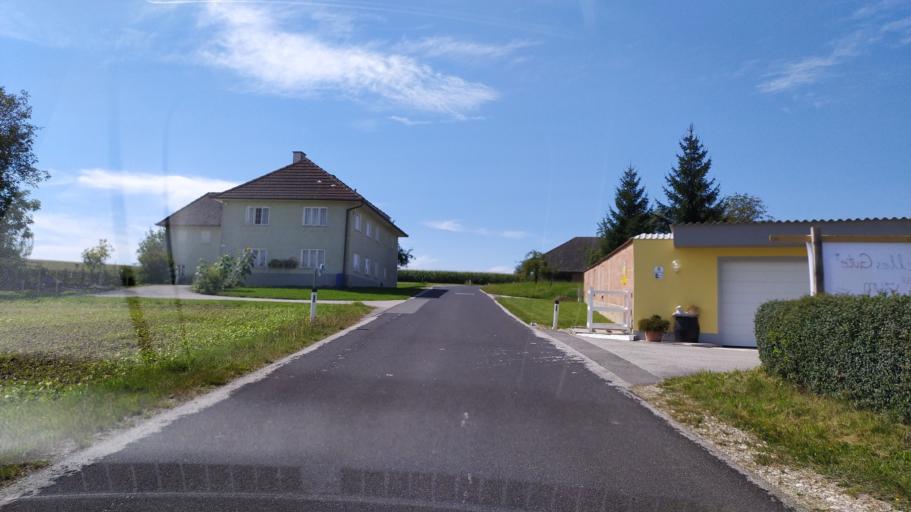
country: AT
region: Lower Austria
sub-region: Politischer Bezirk Amstetten
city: Strengberg
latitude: 48.1115
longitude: 14.6708
